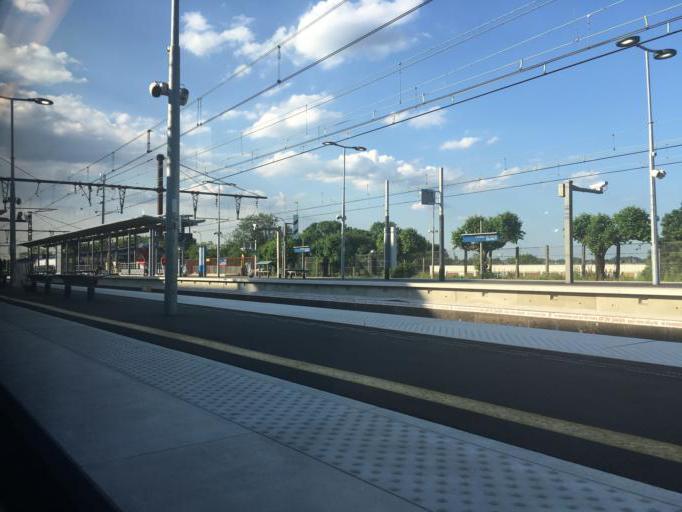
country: FR
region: Ile-de-France
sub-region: Departement de l'Essonne
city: Quincy-sous-Senart
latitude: 48.6670
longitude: 2.5482
